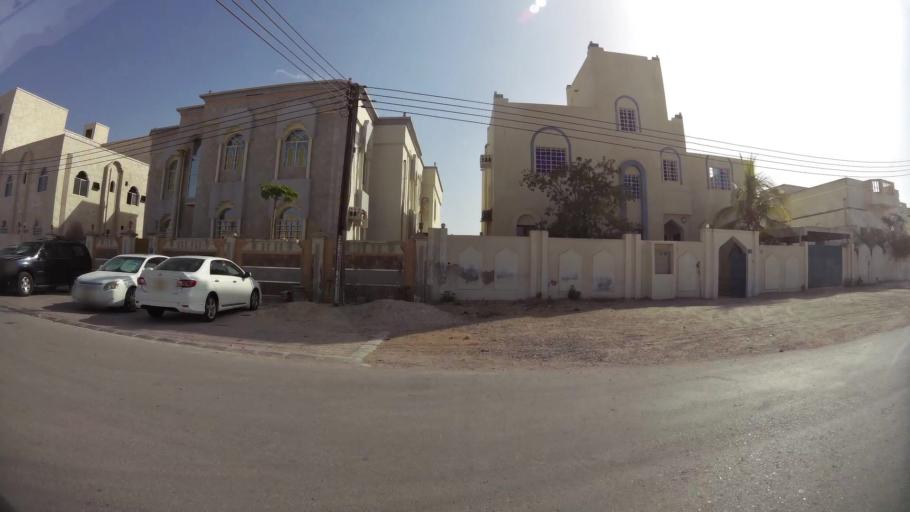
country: OM
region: Zufar
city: Salalah
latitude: 17.0107
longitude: 54.0159
